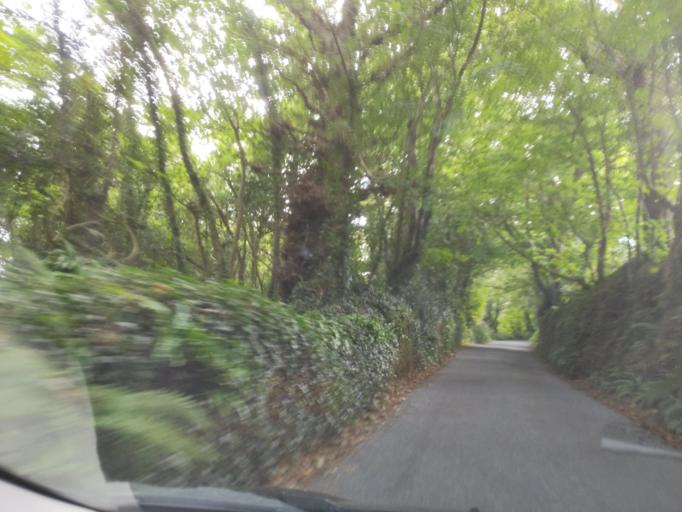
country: GB
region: England
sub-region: Plymouth
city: Plymstock
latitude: 50.3494
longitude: -4.1078
